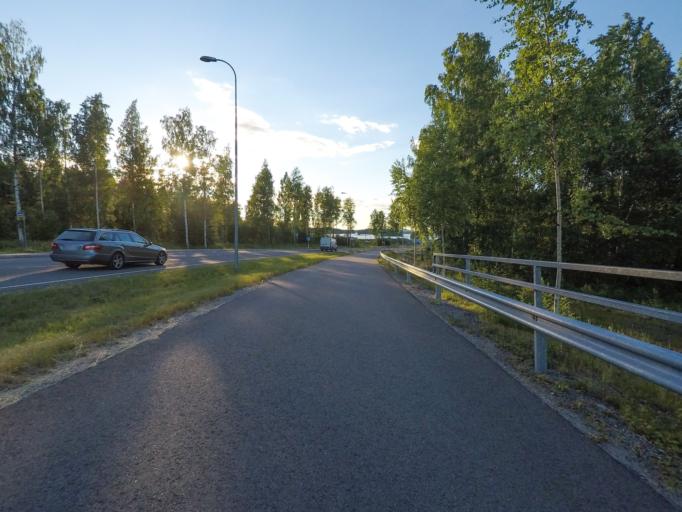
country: FI
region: Northern Savo
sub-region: Kuopio
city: Kuopio
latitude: 62.9354
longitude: 27.6693
